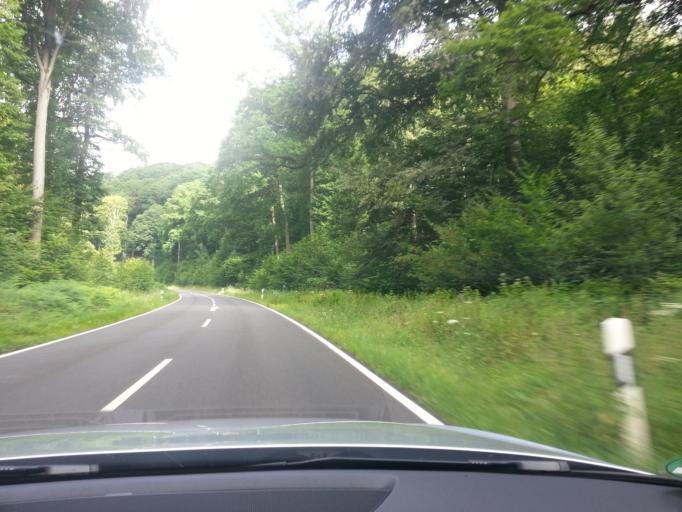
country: DE
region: Saarland
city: Schmelz
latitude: 49.4712
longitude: 6.7998
